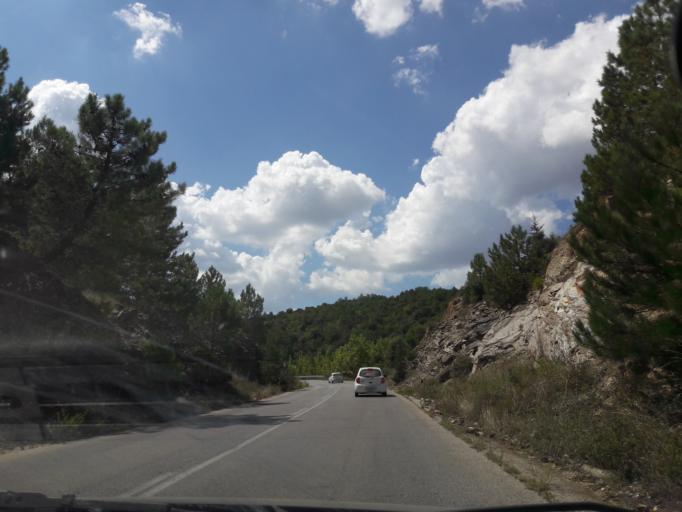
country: GR
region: Central Macedonia
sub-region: Nomos Chalkidikis
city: Polygyros
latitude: 40.3618
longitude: 23.4949
